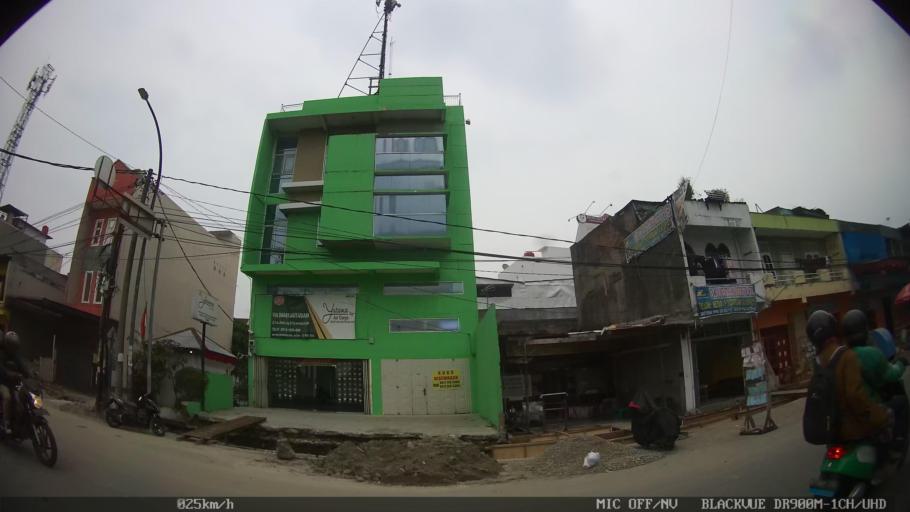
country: ID
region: North Sumatra
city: Medan
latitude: 3.5687
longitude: 98.6915
